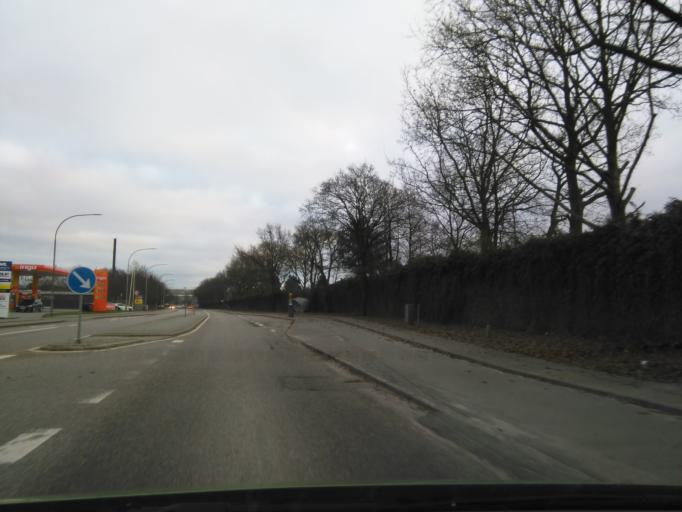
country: DK
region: Central Jutland
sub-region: Arhus Kommune
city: Stavtrup
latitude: 56.1626
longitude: 10.1252
